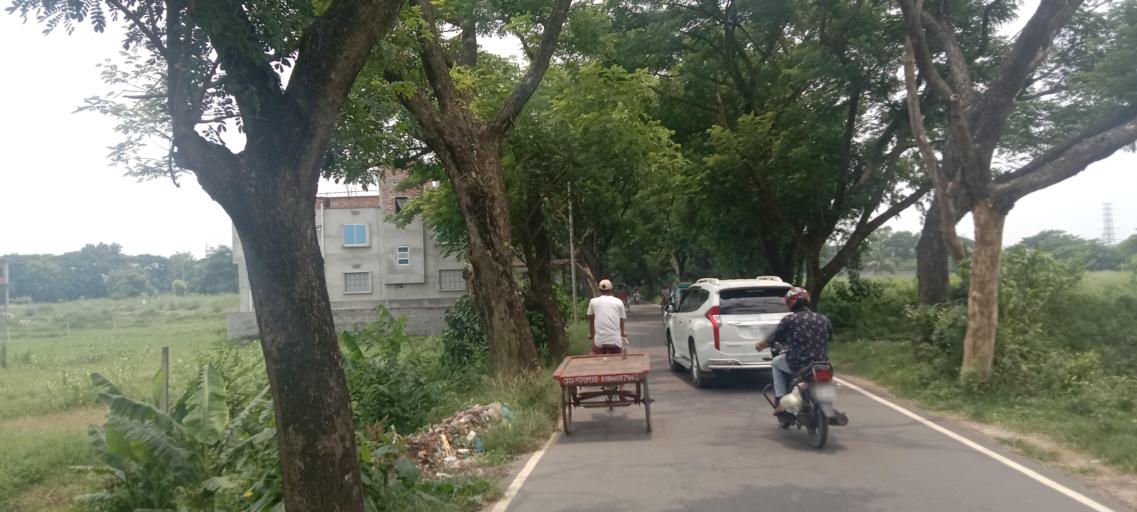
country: BD
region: Dhaka
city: Azimpur
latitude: 23.7152
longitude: 90.3447
